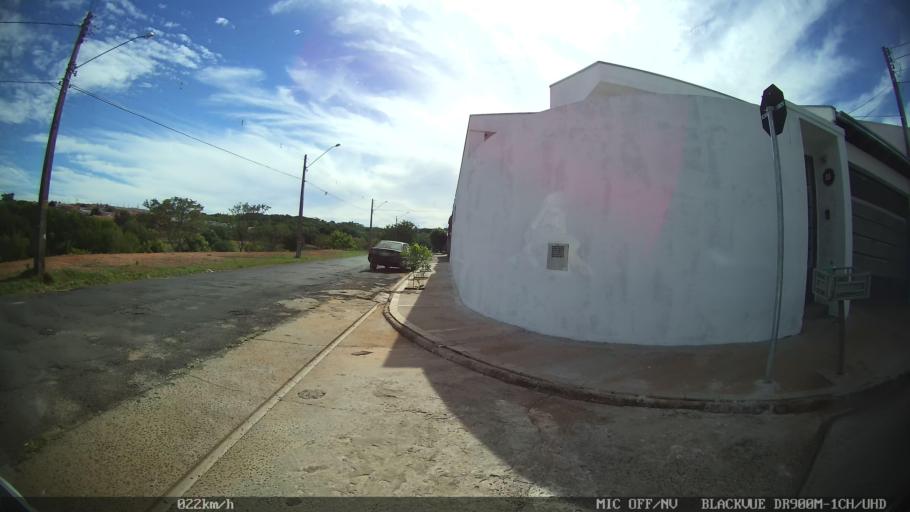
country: BR
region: Sao Paulo
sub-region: Catanduva
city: Catanduva
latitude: -21.1276
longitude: -48.9426
